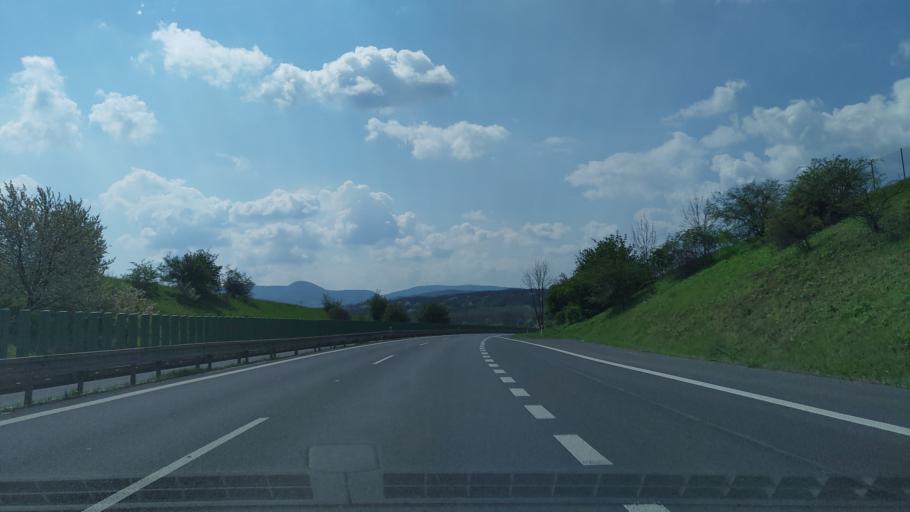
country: CZ
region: Ustecky
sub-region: Okres Teplice
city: Teplice
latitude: 50.6170
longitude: 13.8342
